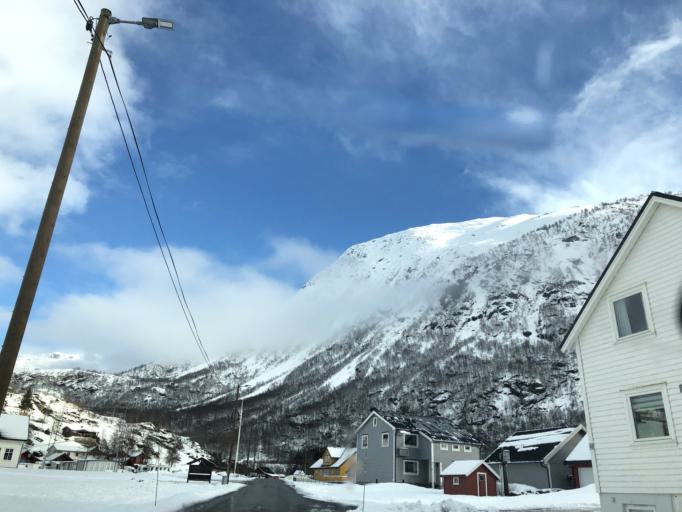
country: NO
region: Hordaland
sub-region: Odda
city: Odda
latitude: 59.8310
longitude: 6.8237
